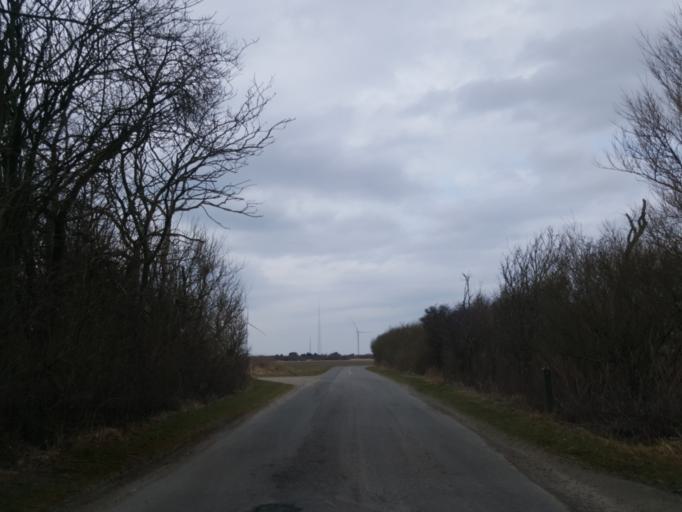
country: DK
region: Central Jutland
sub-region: Lemvig Kommune
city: Lemvig
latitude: 56.4368
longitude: 8.1786
